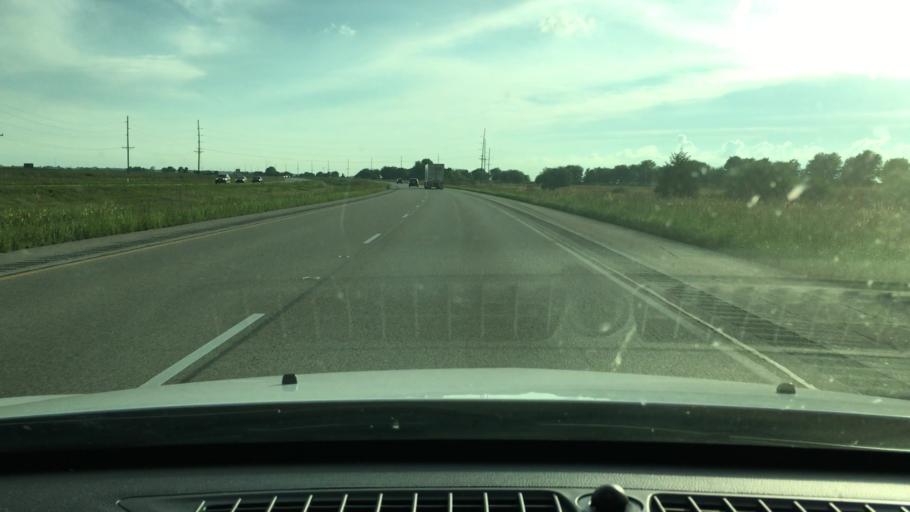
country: US
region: Illinois
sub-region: Logan County
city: Atlanta
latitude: 40.3048
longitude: -89.1781
